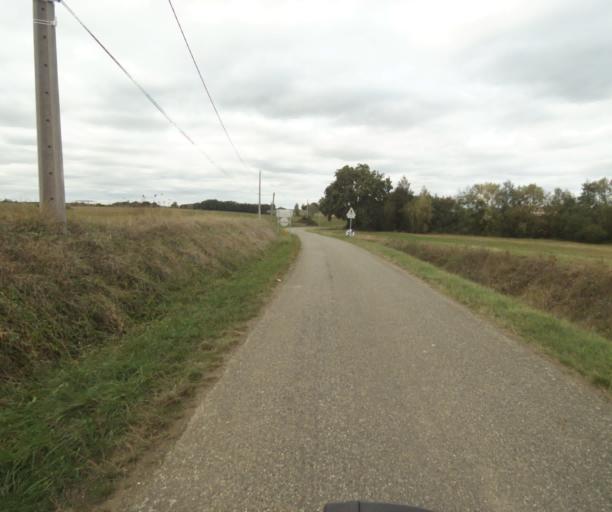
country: FR
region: Midi-Pyrenees
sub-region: Departement du Tarn-et-Garonne
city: Verdun-sur-Garonne
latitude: 43.8634
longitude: 1.1745
